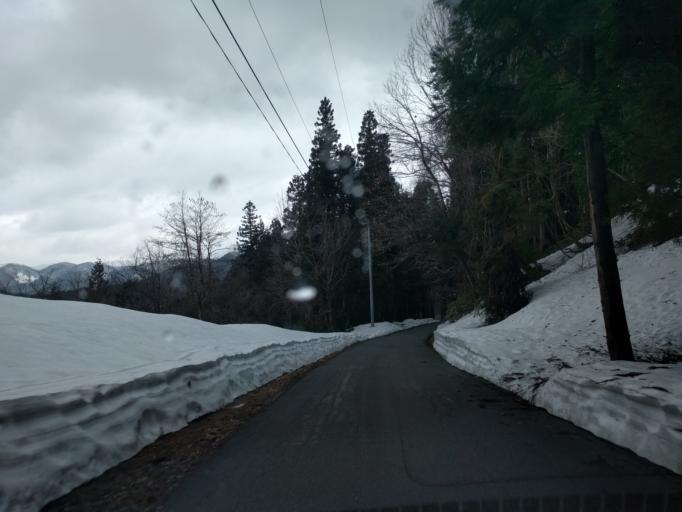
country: JP
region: Fukushima
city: Kitakata
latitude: 37.6926
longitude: 139.9457
